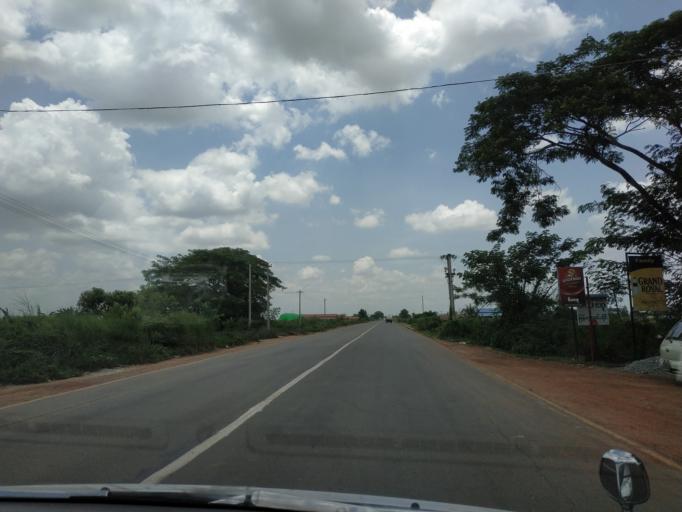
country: MM
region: Bago
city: Bago
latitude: 17.4710
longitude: 96.5513
